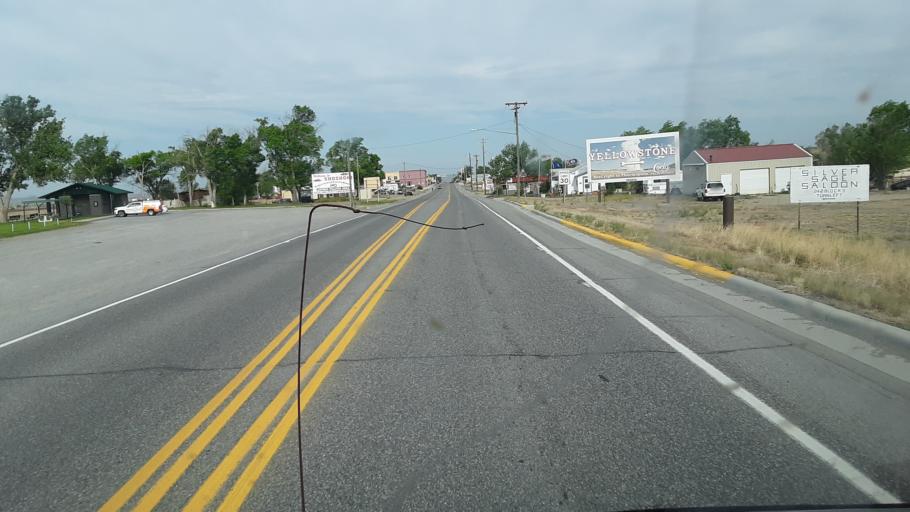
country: US
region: Wyoming
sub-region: Fremont County
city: Riverton
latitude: 43.2356
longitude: -108.1025
